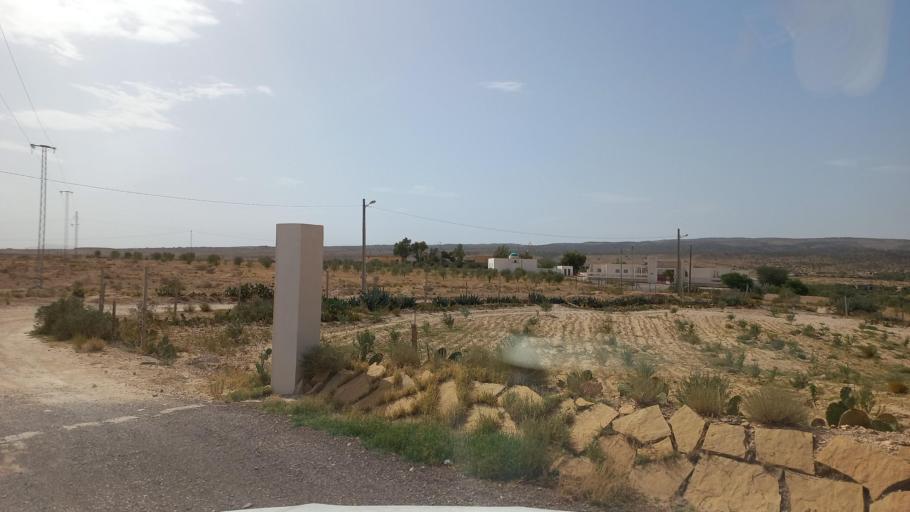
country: TN
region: Al Qasrayn
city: Kasserine
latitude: 35.2981
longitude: 8.9528
